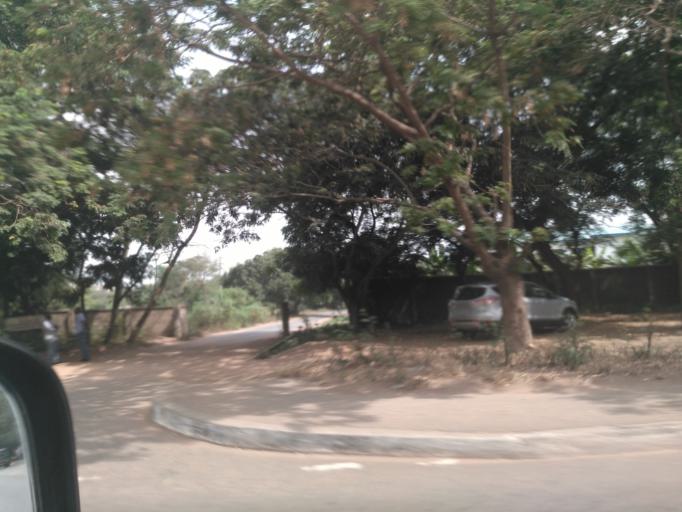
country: GH
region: Greater Accra
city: Accra
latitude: 5.5939
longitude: -0.1864
